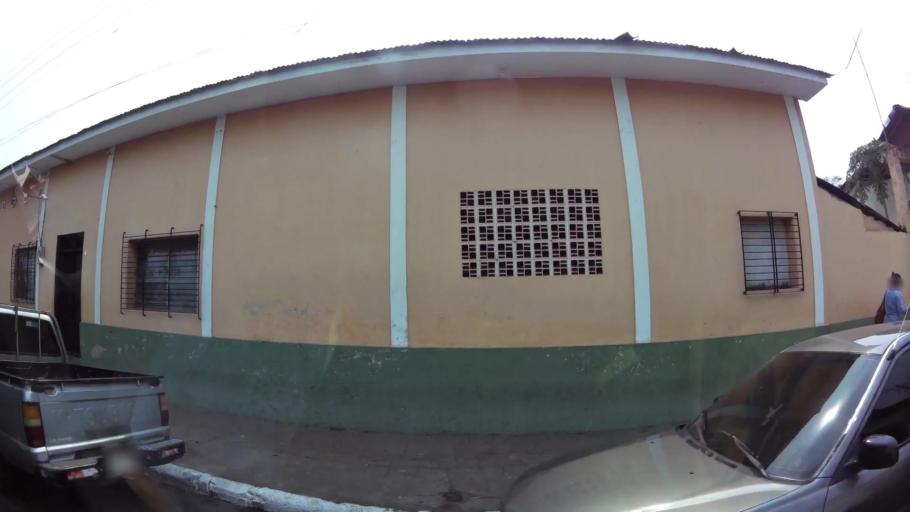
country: NI
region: Chinandega
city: Chinandega
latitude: 12.6327
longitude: -87.1312
